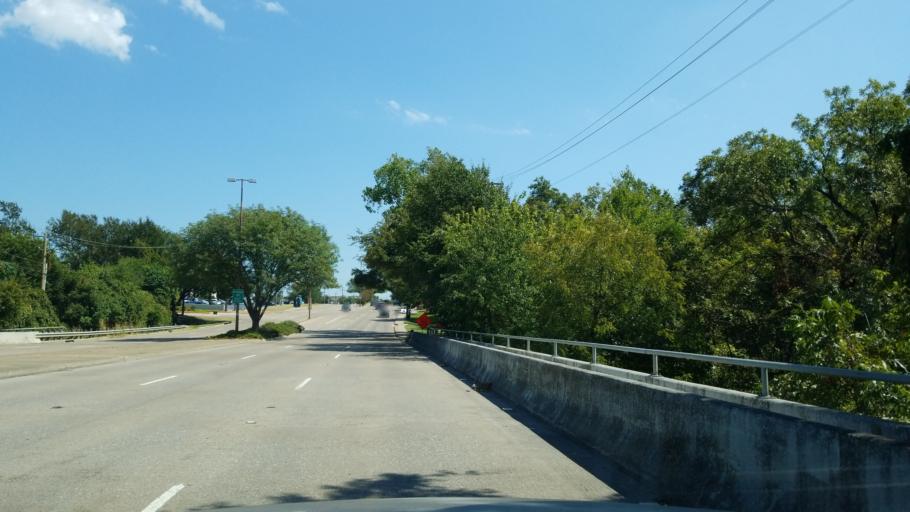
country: US
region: Texas
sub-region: Dallas County
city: Addison
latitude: 32.9540
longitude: -96.8084
